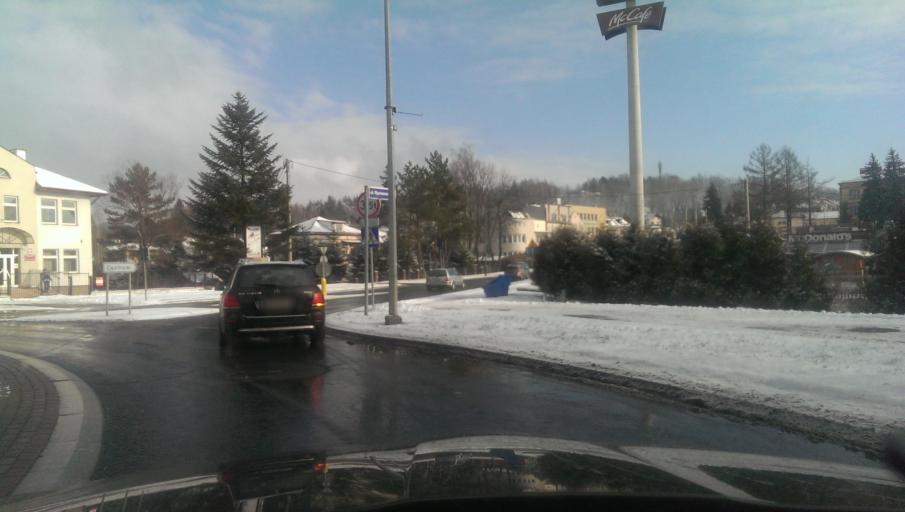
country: PL
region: Subcarpathian Voivodeship
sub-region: Powiat sanocki
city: Sanok
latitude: 49.5619
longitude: 22.1912
